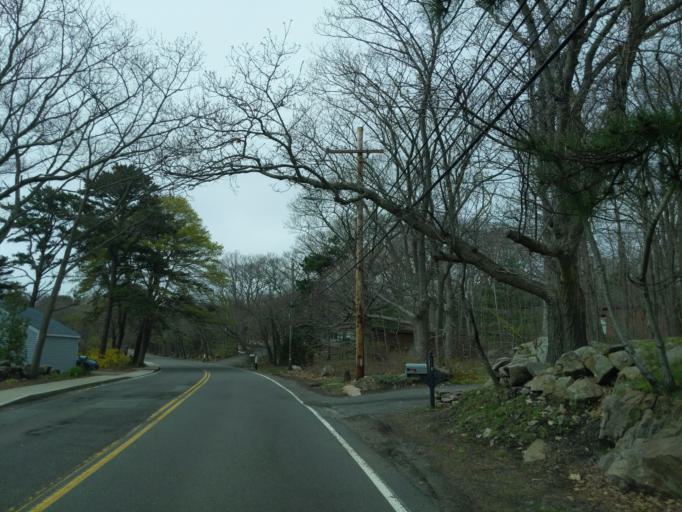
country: US
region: Massachusetts
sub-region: Essex County
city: Rockport
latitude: 42.6450
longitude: -70.5995
